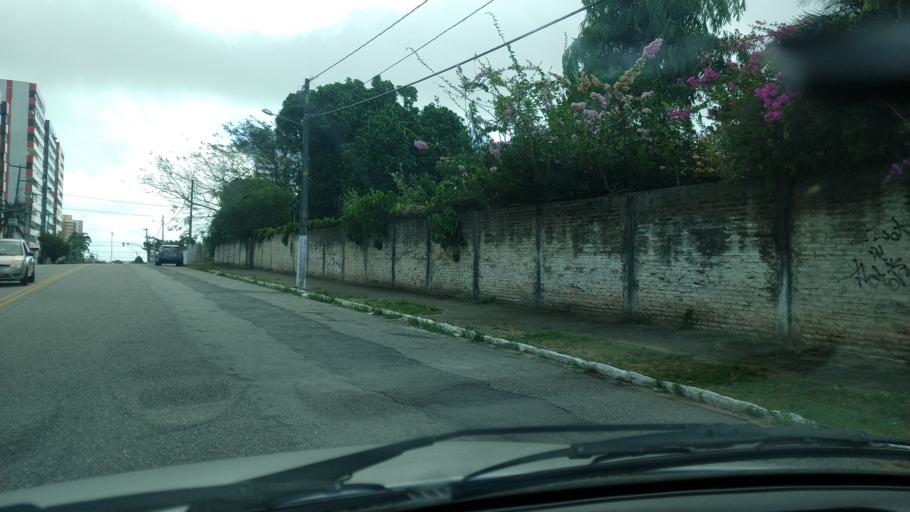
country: BR
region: Rio Grande do Norte
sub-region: Natal
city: Natal
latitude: -5.8148
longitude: -35.2200
